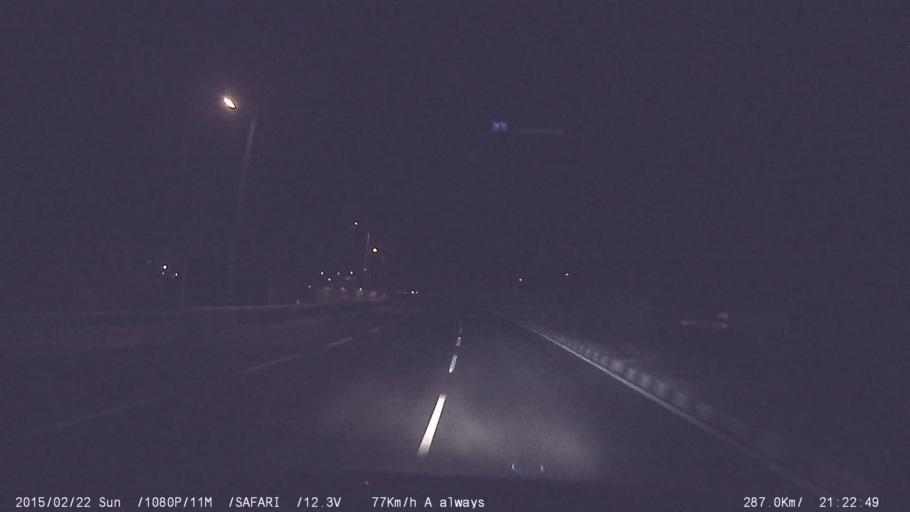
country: IN
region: Tamil Nadu
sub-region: Karur
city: Karur
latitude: 10.8749
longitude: 78.0044
